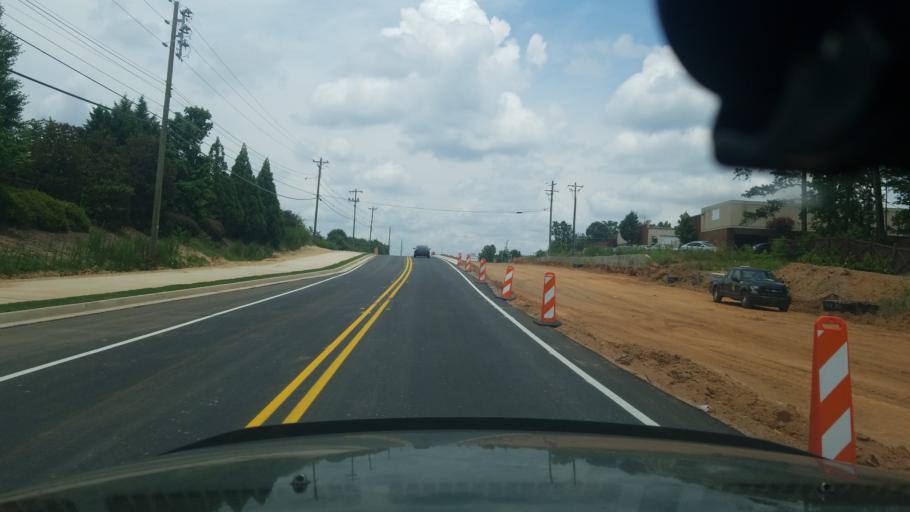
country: US
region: Georgia
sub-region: Fulton County
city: Milton
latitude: 34.1221
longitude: -84.2336
